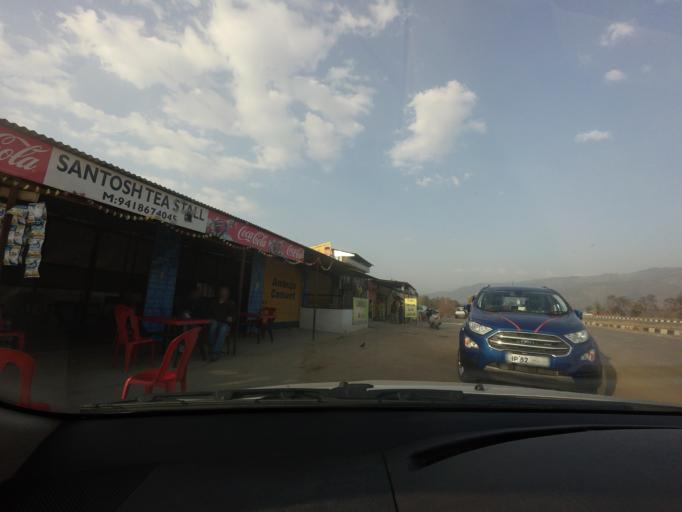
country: IN
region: Himachal Pradesh
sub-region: Mandi
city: Sundarnagar
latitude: 31.6039
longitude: 76.9256
